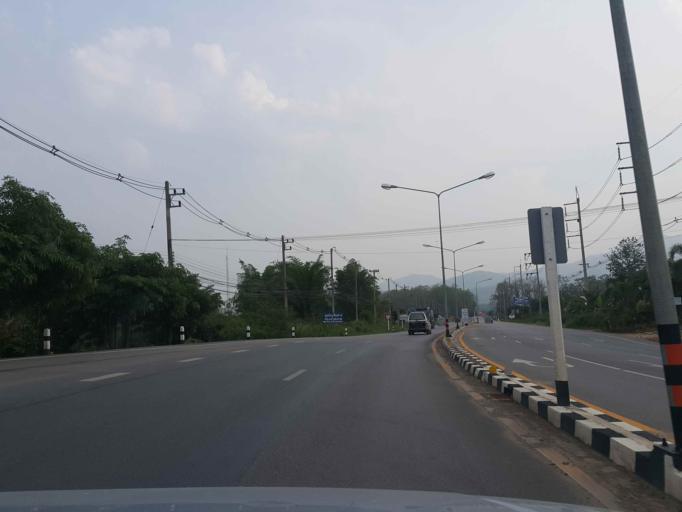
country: TH
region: Chiang Mai
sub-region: Amphoe Chiang Dao
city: Chiang Dao
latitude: 19.3433
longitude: 98.9605
